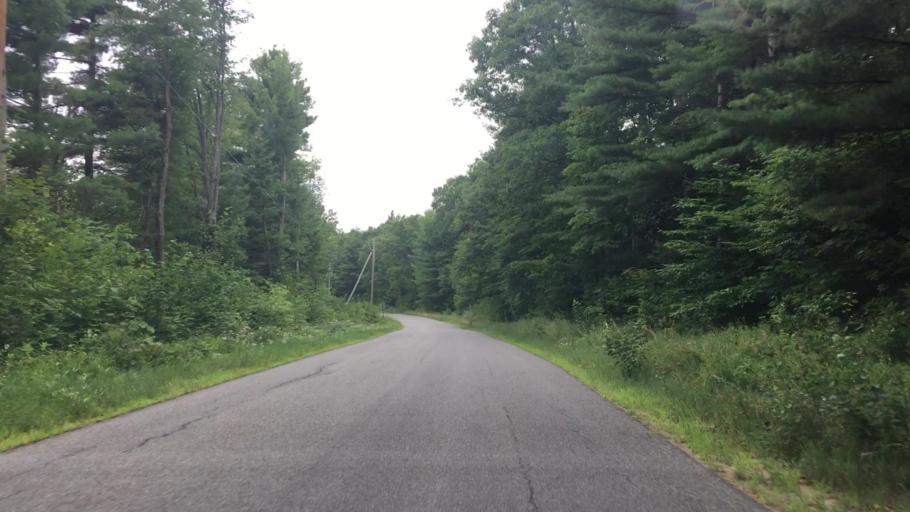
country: US
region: New York
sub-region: Essex County
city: Keeseville
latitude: 44.4505
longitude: -73.5961
